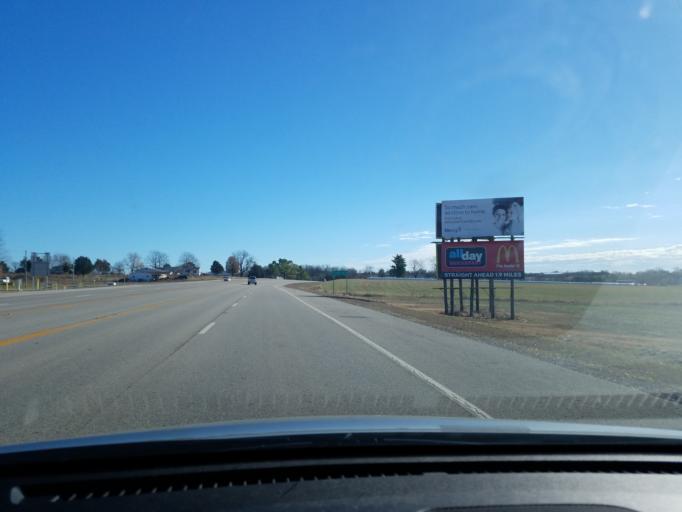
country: US
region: Arkansas
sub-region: Carroll County
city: Berryville
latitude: 36.3900
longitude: -93.6205
